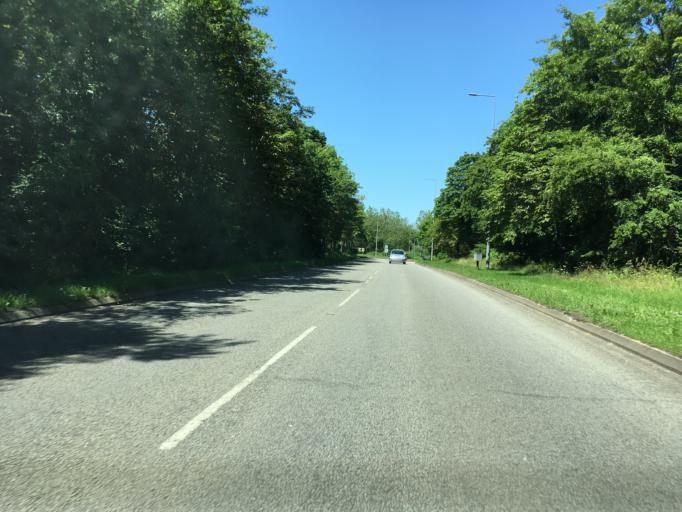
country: GB
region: England
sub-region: Milton Keynes
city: Milton Keynes
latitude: 52.0407
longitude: -0.7423
